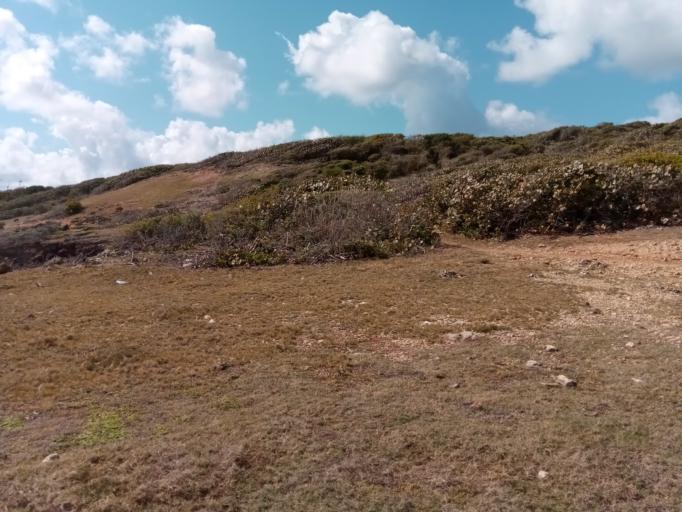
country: GP
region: Guadeloupe
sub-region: Guadeloupe
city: Saint-Francois
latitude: 16.2771
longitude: -61.2458
